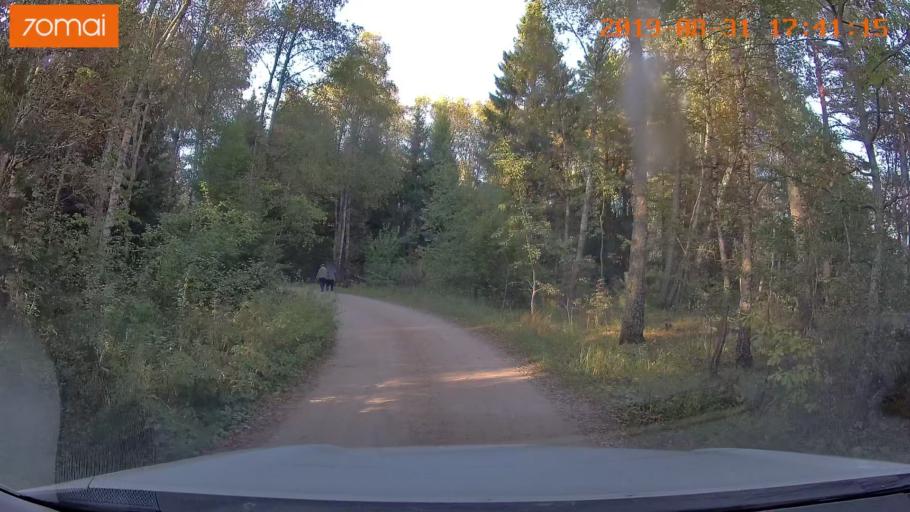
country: RU
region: Kaluga
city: Detchino
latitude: 54.8201
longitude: 36.3656
